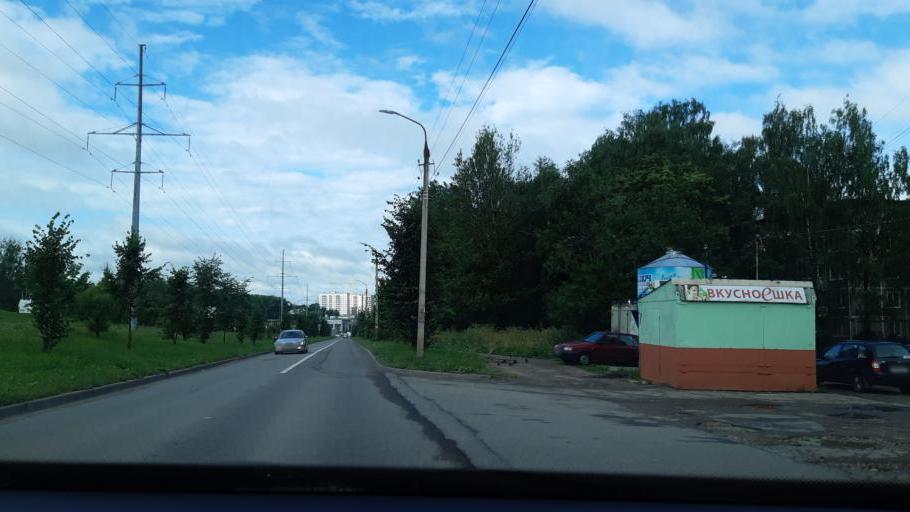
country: RU
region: Smolensk
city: Smolensk
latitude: 54.7634
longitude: 32.0881
